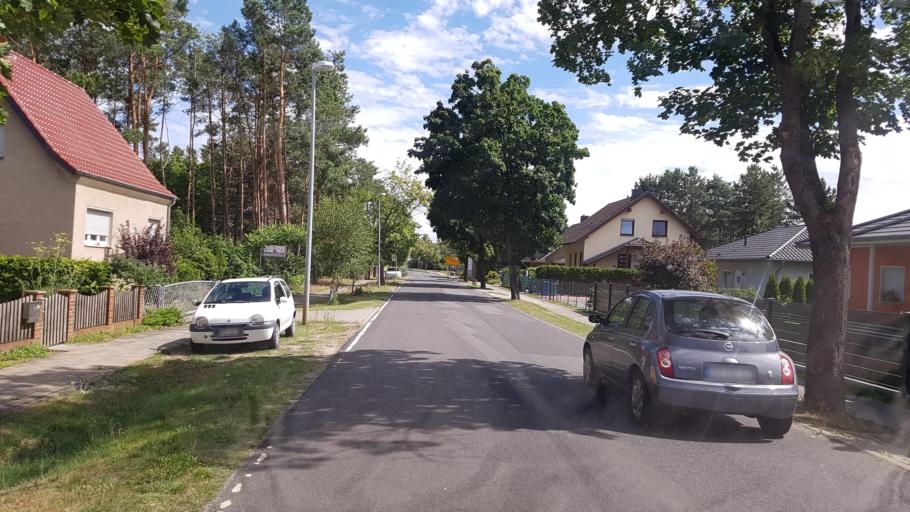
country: DE
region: Brandenburg
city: Luckenwalde
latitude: 52.1186
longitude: 13.1922
